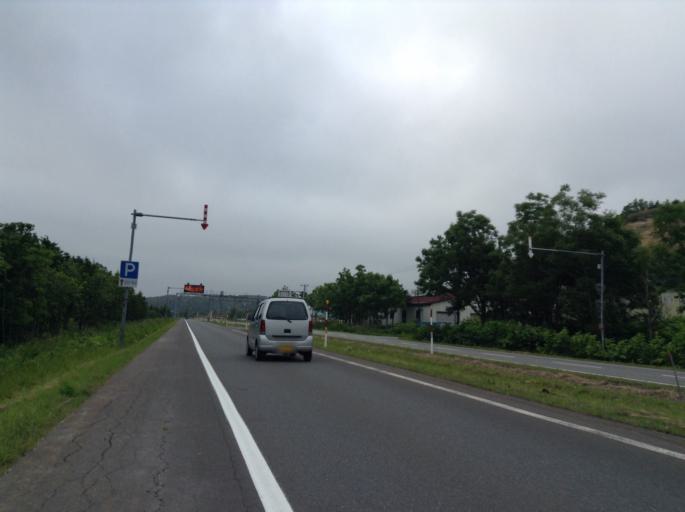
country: JP
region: Hokkaido
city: Wakkanai
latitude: 45.3661
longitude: 141.7285
